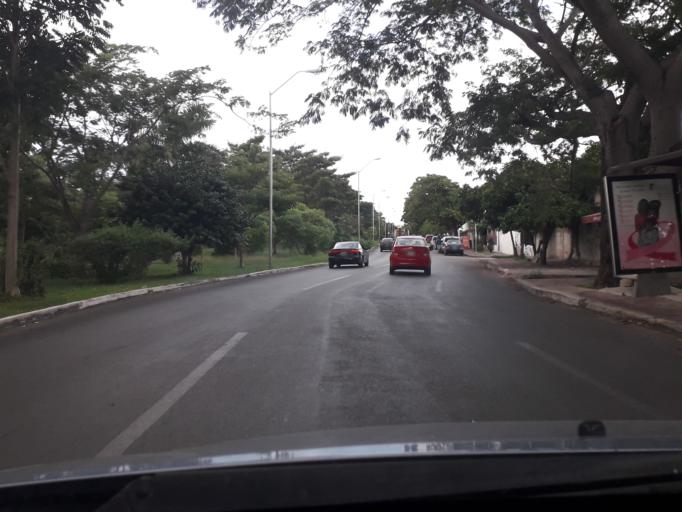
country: MX
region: Yucatan
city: Merida
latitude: 20.9831
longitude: -89.6633
